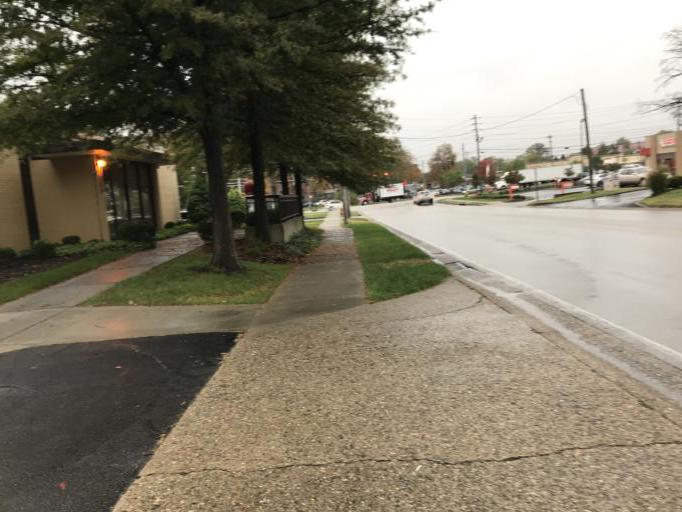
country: US
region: Kentucky
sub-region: Jefferson County
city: West Buechel
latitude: 38.2006
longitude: -85.6838
